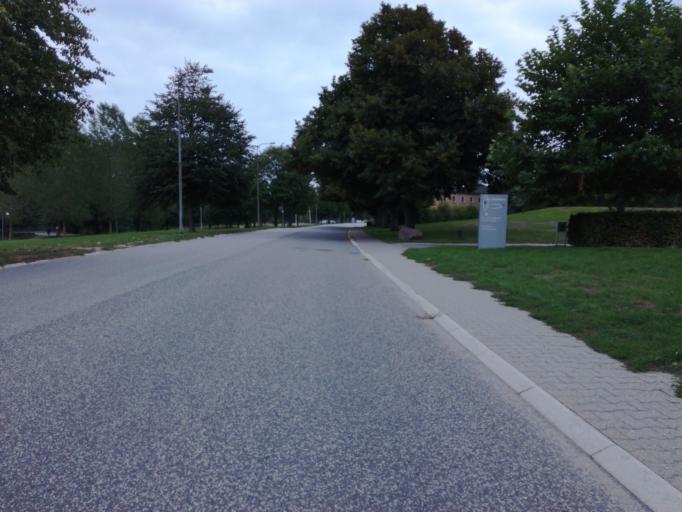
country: DK
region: South Denmark
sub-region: Fredericia Kommune
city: Fredericia
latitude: 55.5722
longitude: 9.7321
